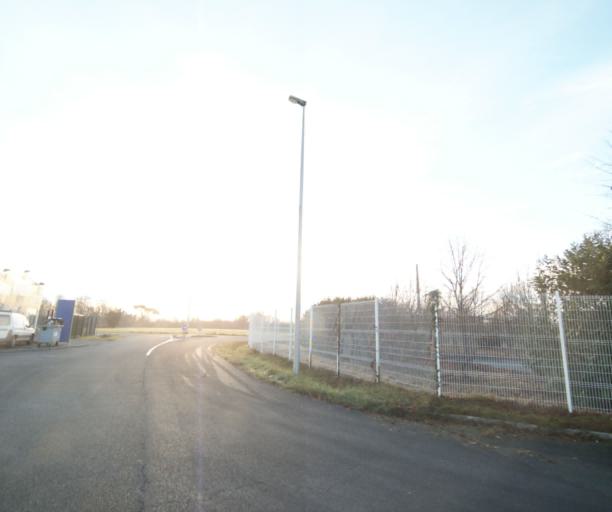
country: FR
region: Poitou-Charentes
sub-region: Departement de la Charente-Maritime
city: Fontcouverte
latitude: 45.7711
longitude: -0.5765
